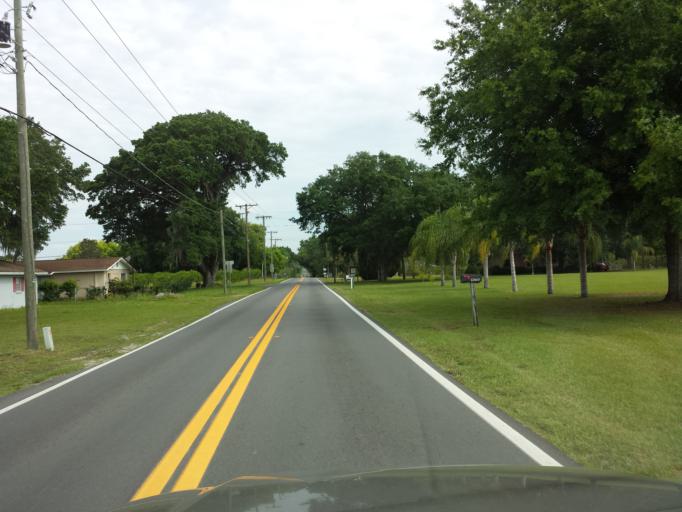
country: US
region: Florida
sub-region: Pasco County
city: San Antonio
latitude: 28.3460
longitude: -82.2744
